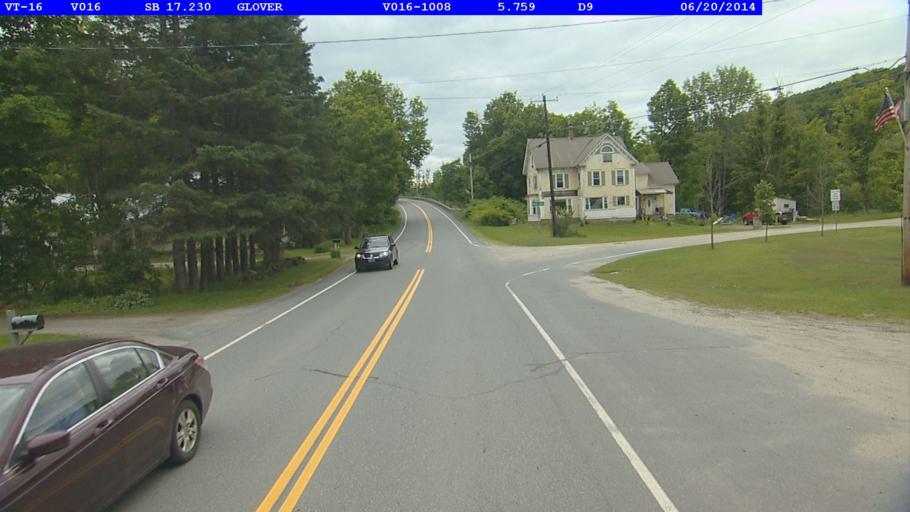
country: US
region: Vermont
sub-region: Orleans County
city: Newport
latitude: 44.7042
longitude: -72.1886
